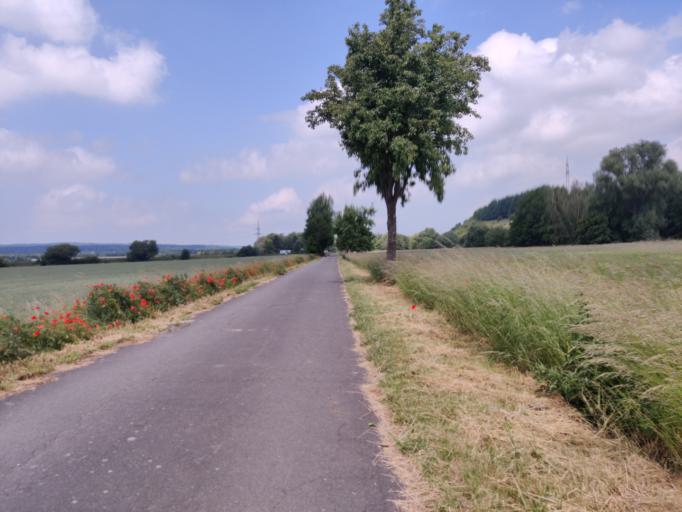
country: DE
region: Lower Saxony
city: Hildesheim
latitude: 52.1215
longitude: 9.9724
